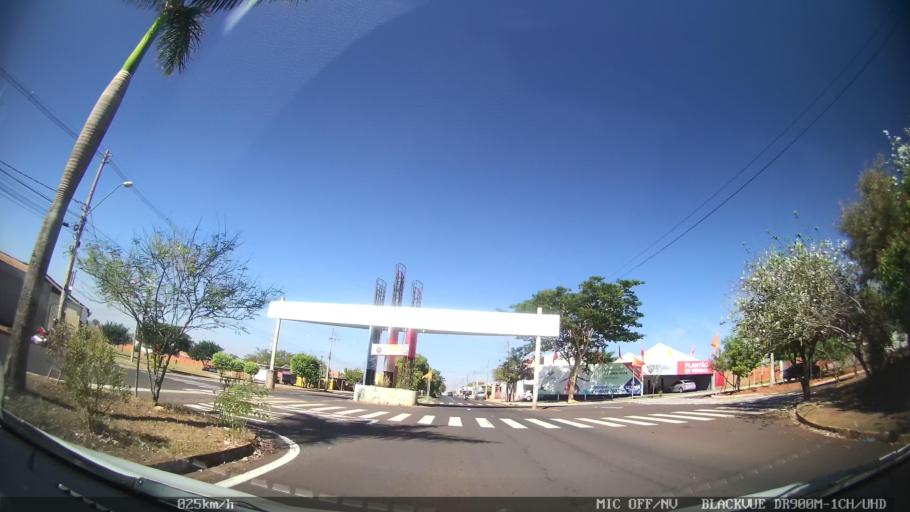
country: BR
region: Sao Paulo
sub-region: Sao Jose Do Rio Preto
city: Sao Jose do Rio Preto
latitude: -20.7465
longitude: -49.4082
